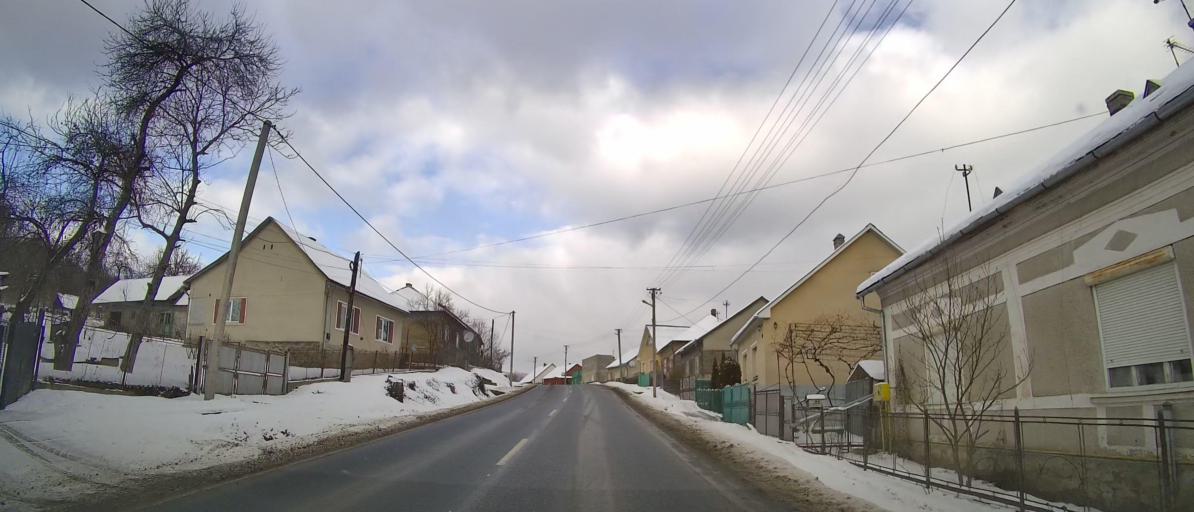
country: UA
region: Zakarpattia
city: Velykyi Bereznyi
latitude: 48.9115
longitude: 22.4601
